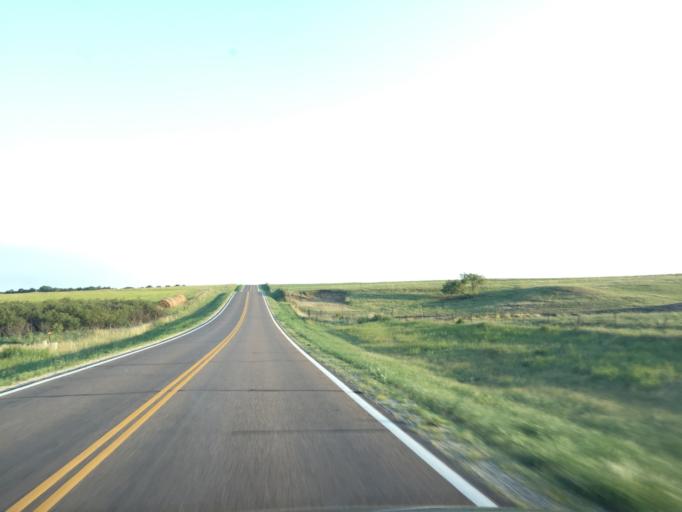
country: US
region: Kansas
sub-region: Ellsworth County
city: Ellsworth
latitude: 38.7846
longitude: -98.2250
